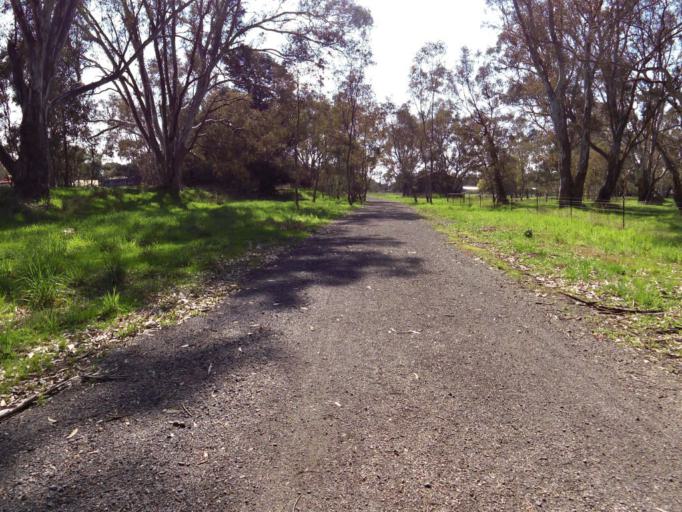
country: AU
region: Victoria
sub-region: Murrindindi
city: Alexandra
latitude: -37.1055
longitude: 145.6159
